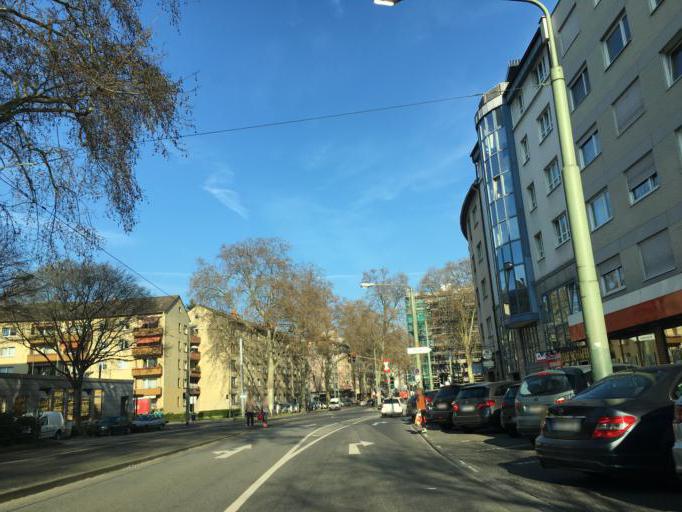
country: DE
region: Hesse
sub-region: Regierungsbezirk Darmstadt
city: Frankfurt am Main
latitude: 50.1129
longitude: 8.7022
